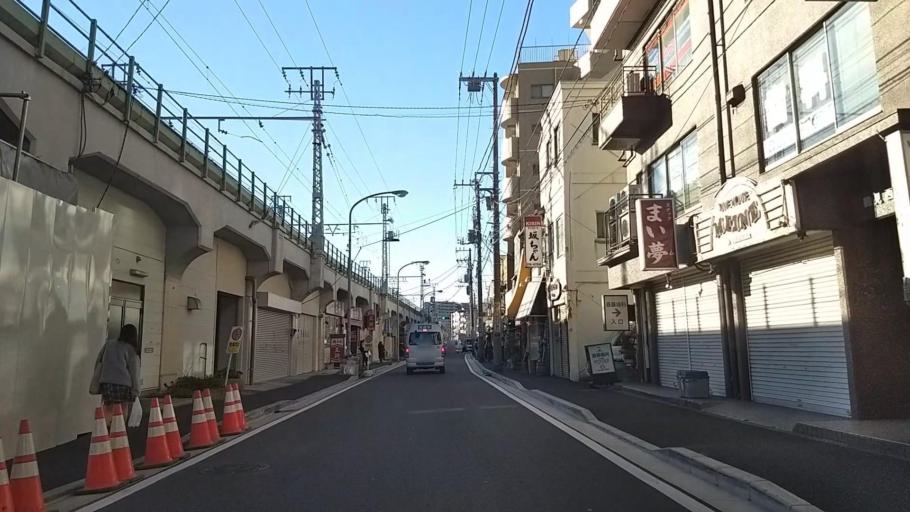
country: JP
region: Kanagawa
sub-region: Kawasaki-shi
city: Kawasaki
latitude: 35.5064
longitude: 139.6754
